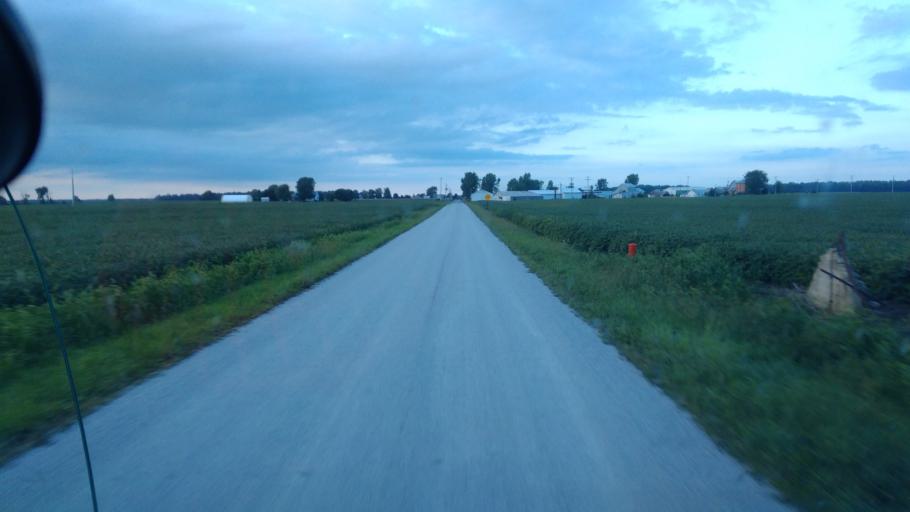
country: US
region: Ohio
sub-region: Hardin County
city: Kenton
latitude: 40.6769
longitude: -83.5145
